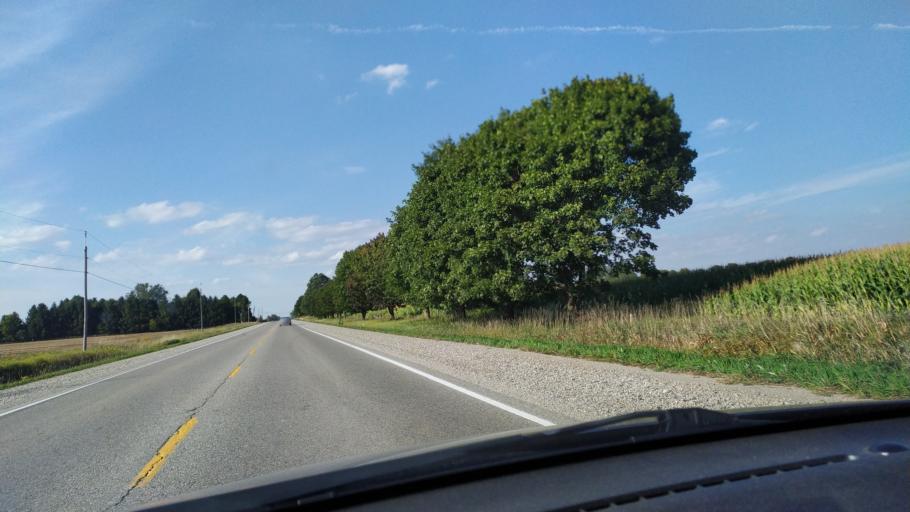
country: CA
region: Ontario
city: Ingersoll
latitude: 43.1127
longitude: -80.8799
